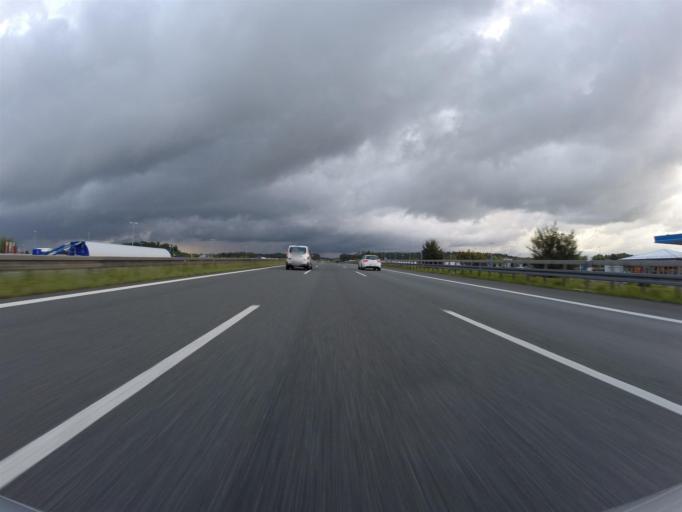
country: DE
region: Bavaria
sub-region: Upper Franconia
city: Pegnitz
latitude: 49.7467
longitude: 11.5127
